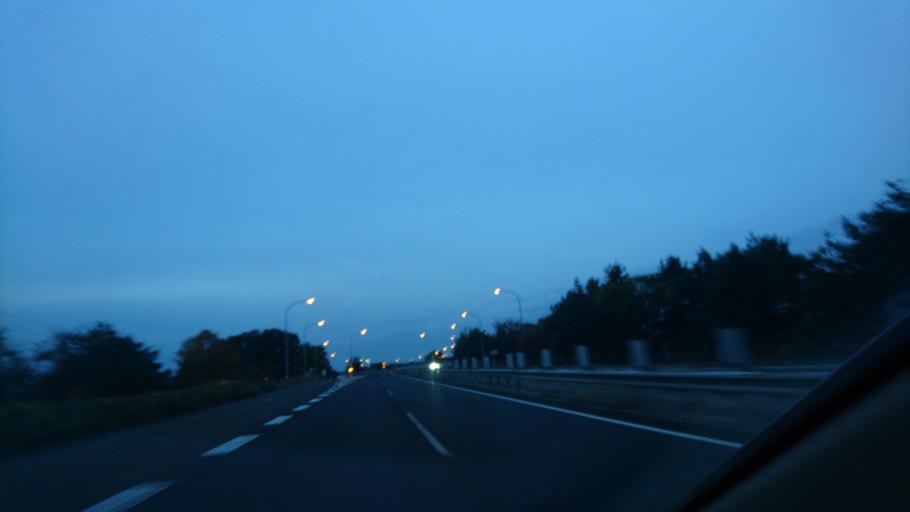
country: JP
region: Iwate
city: Morioka-shi
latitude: 39.6223
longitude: 141.1296
